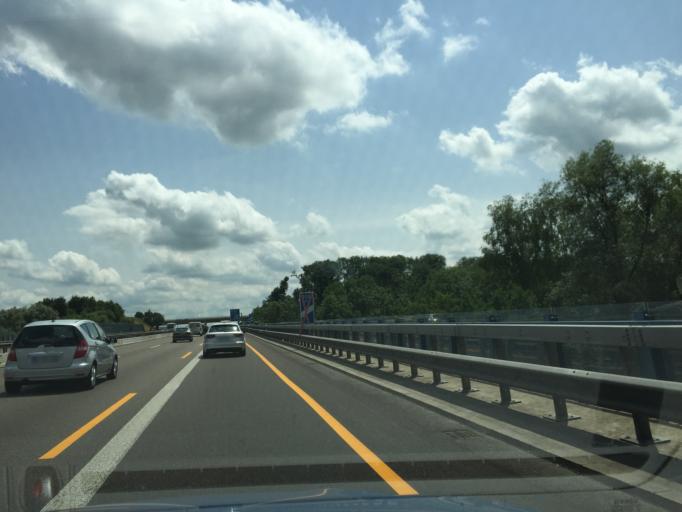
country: DE
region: Bavaria
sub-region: Swabia
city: Leipheim
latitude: 48.4476
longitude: 10.2055
